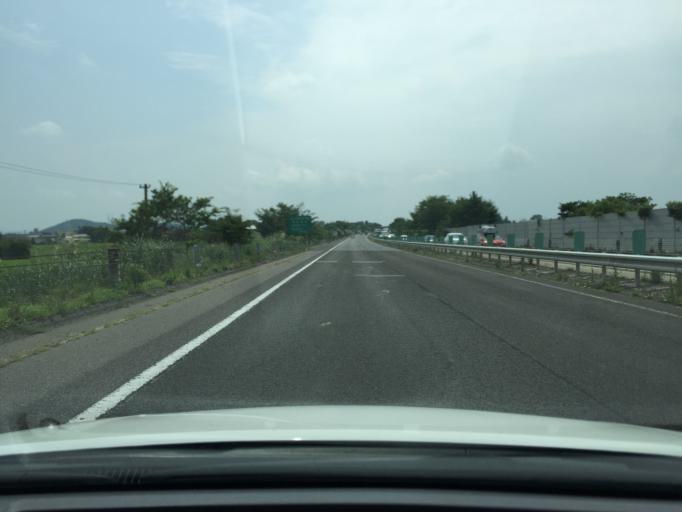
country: JP
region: Fukushima
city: Motomiya
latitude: 37.5039
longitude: 140.3811
